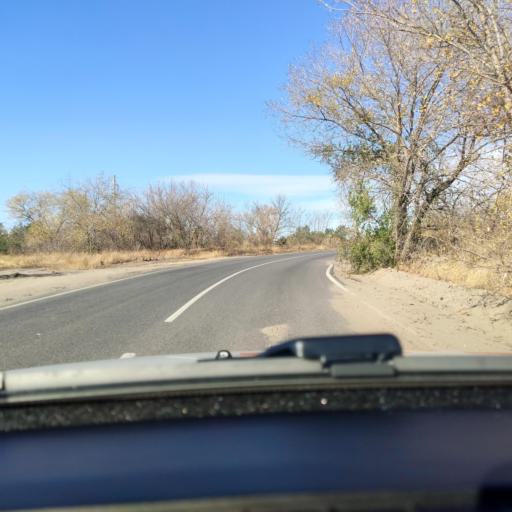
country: RU
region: Voronezj
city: Shilovo
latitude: 51.5523
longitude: 39.1332
